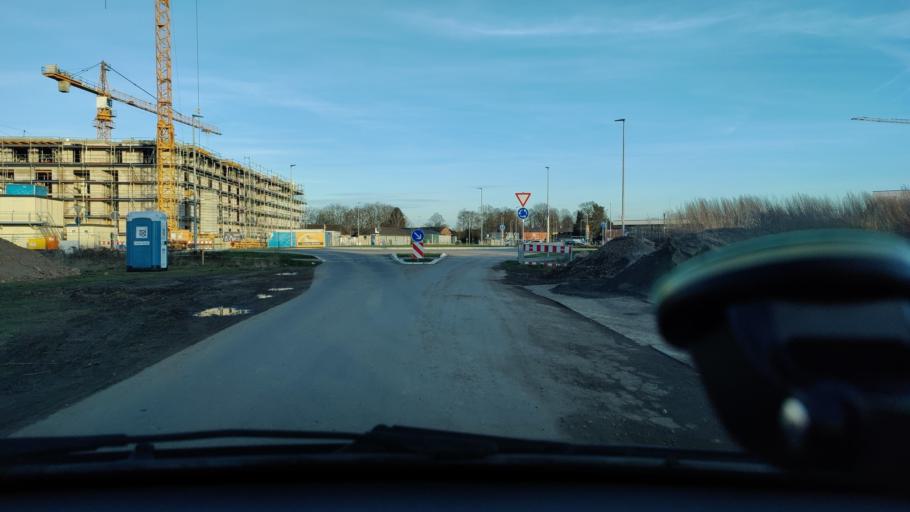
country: DE
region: North Rhine-Westphalia
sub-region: Regierungsbezirk Dusseldorf
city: Goch
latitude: 51.6854
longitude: 6.1630
